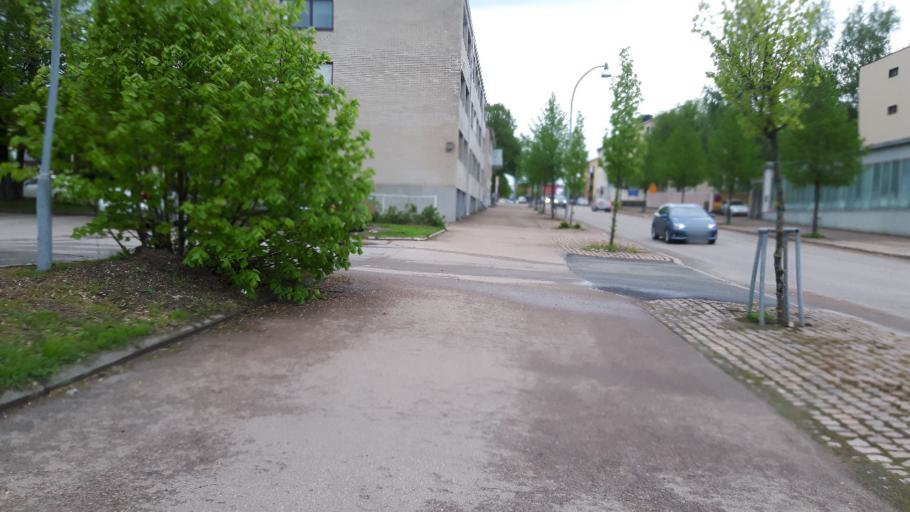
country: FI
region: Kymenlaakso
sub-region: Kotka-Hamina
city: Hamina
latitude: 60.5661
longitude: 27.1906
